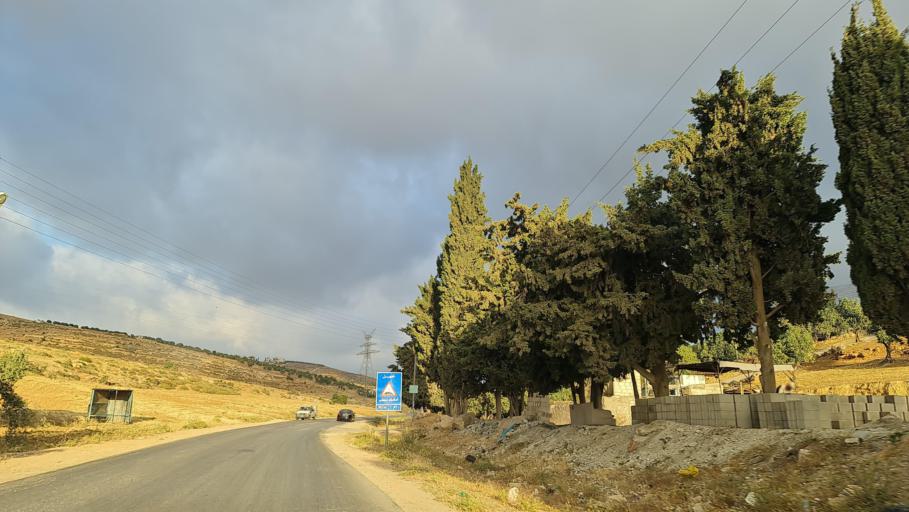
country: JO
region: Amman
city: Al Jubayhah
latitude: 32.0930
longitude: 35.9237
